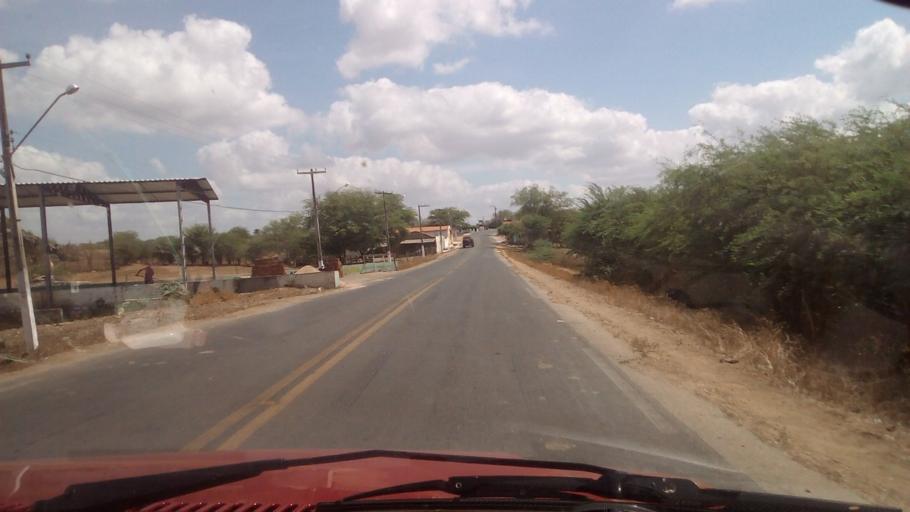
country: BR
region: Paraiba
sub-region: Dona Ines
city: Dona Ines
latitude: -6.5395
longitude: -35.6584
